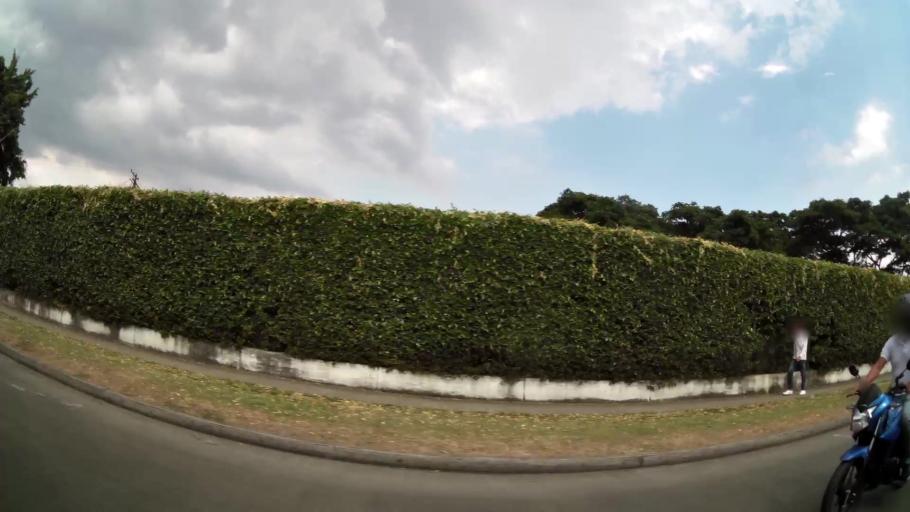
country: CO
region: Valle del Cauca
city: Cali
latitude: 3.4582
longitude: -76.5066
